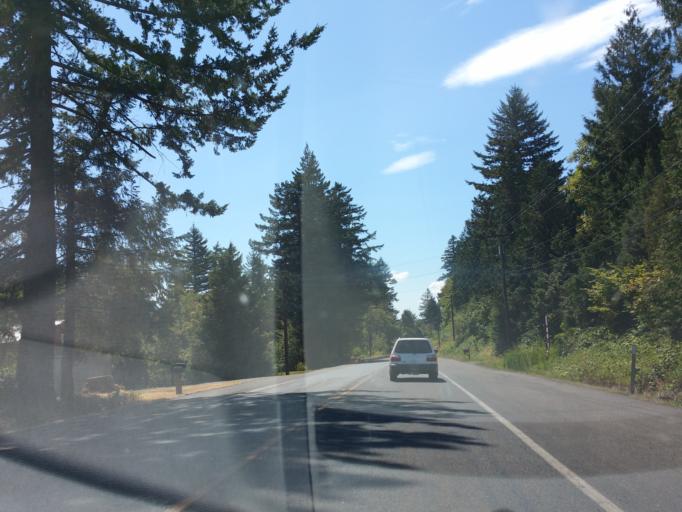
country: US
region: Washington
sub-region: Clark County
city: Washougal
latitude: 45.5938
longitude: -122.1362
